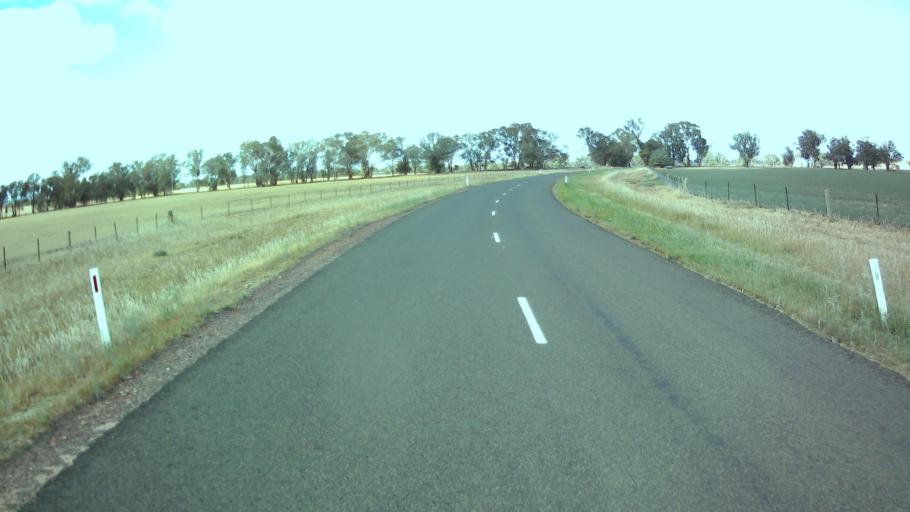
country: AU
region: New South Wales
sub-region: Weddin
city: Grenfell
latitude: -33.9637
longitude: 148.4329
